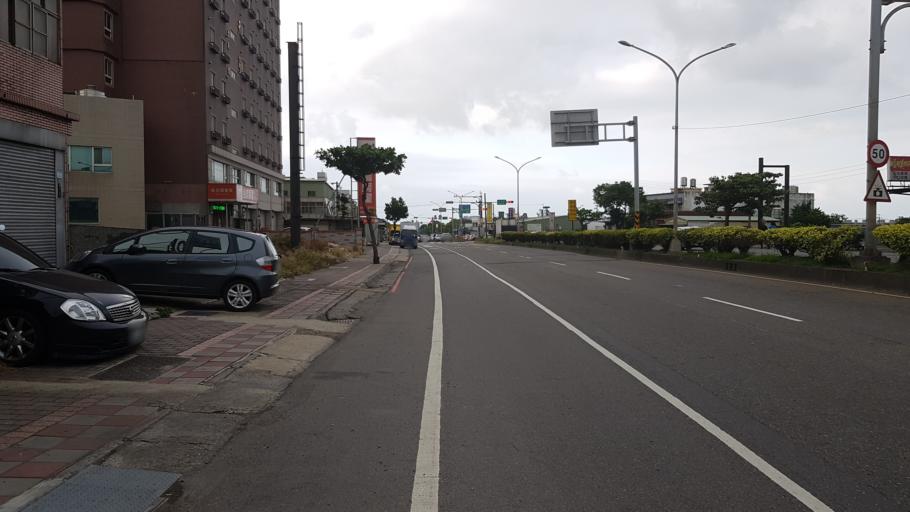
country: TW
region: Taiwan
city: Taoyuan City
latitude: 25.0773
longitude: 121.2598
